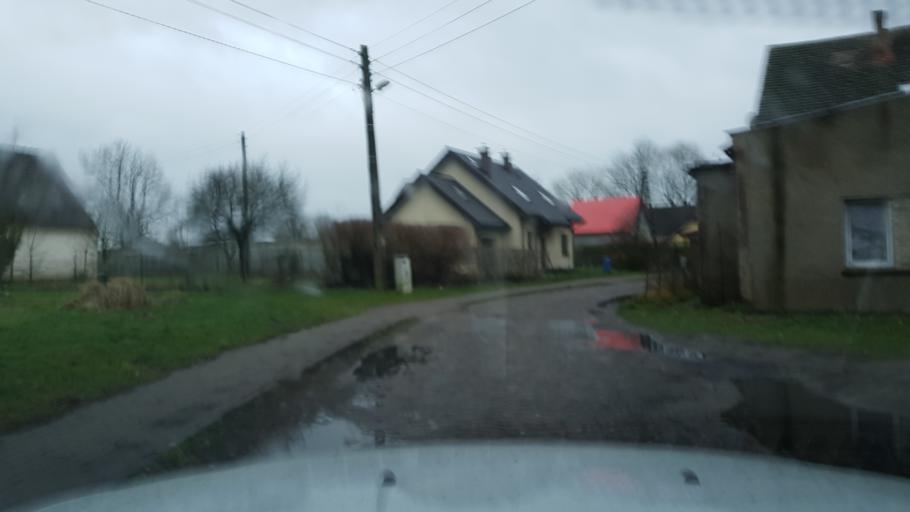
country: PL
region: West Pomeranian Voivodeship
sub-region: Powiat gryficki
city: Brojce
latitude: 53.9904
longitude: 15.3149
